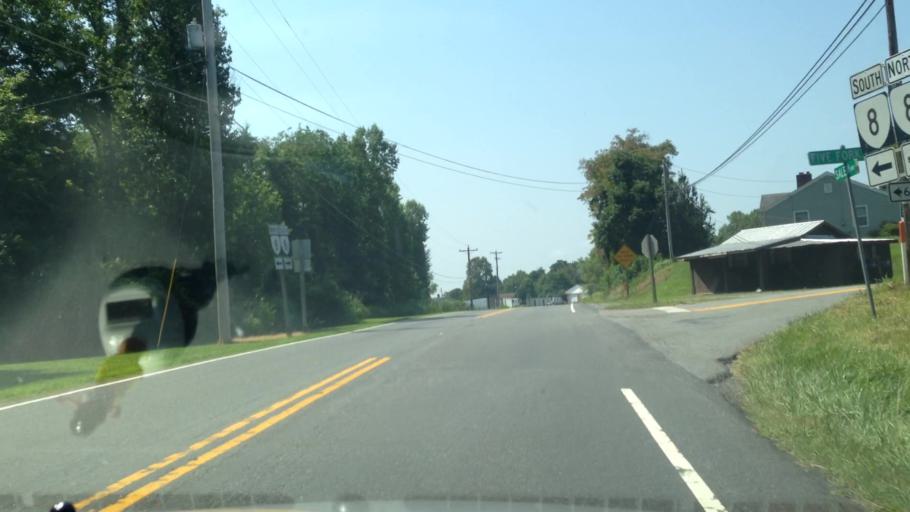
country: US
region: Virginia
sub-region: Patrick County
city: Stuart
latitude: 36.5845
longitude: -80.2785
